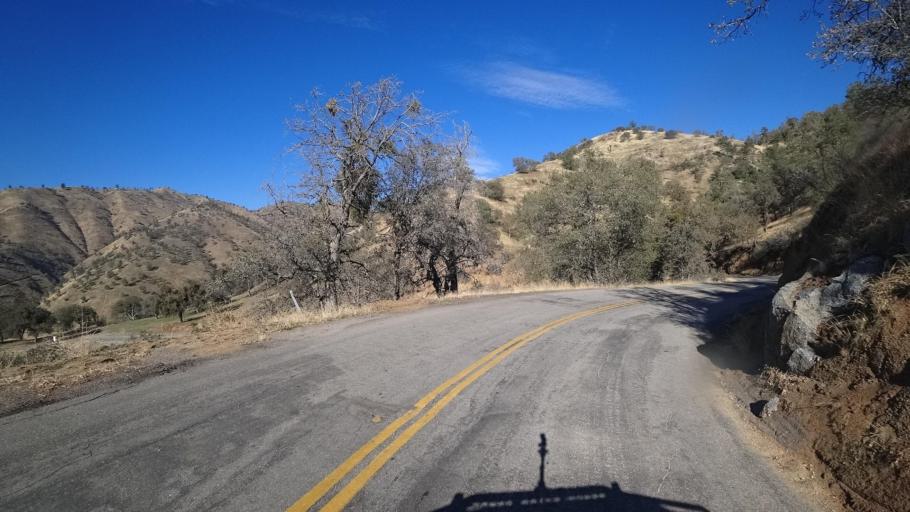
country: US
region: California
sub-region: Kern County
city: Bear Valley Springs
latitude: 35.3377
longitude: -118.5788
